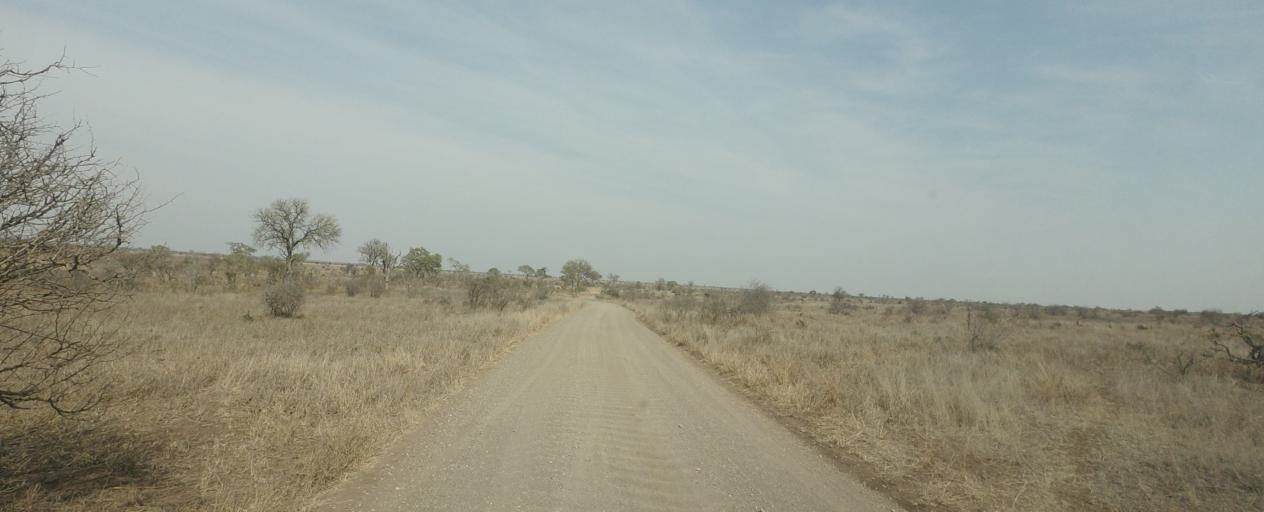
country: ZA
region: Limpopo
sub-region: Mopani District Municipality
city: Phalaborwa
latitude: -24.2604
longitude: 31.7274
